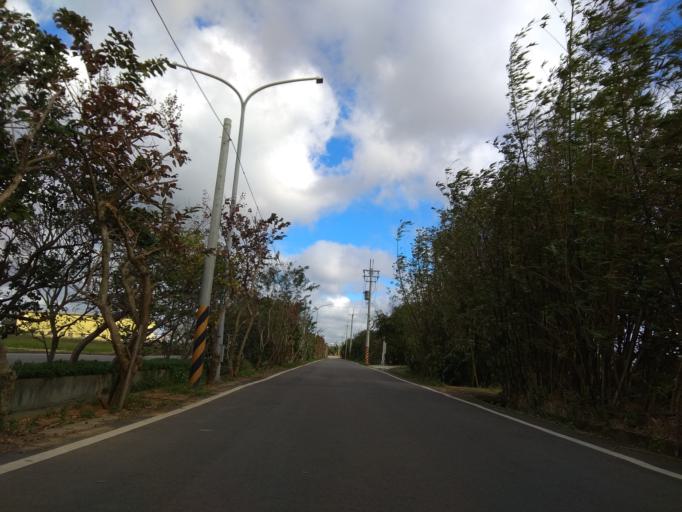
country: TW
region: Taiwan
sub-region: Hsinchu
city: Zhubei
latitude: 24.9739
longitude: 121.0891
